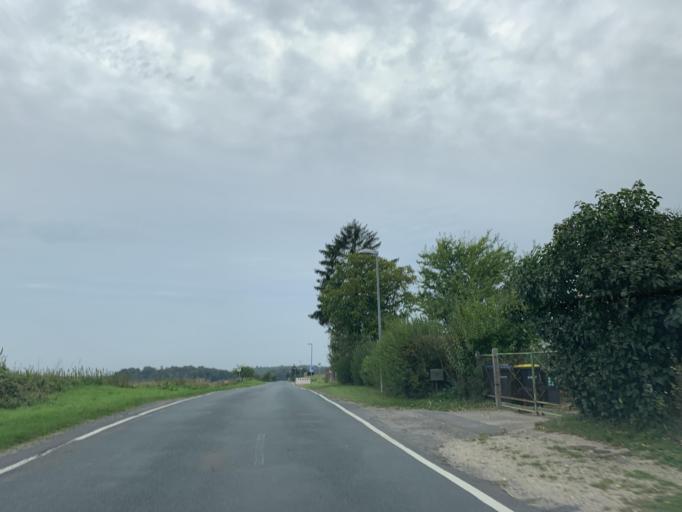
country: DE
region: Mecklenburg-Vorpommern
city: Woldegk
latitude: 53.3339
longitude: 13.6414
